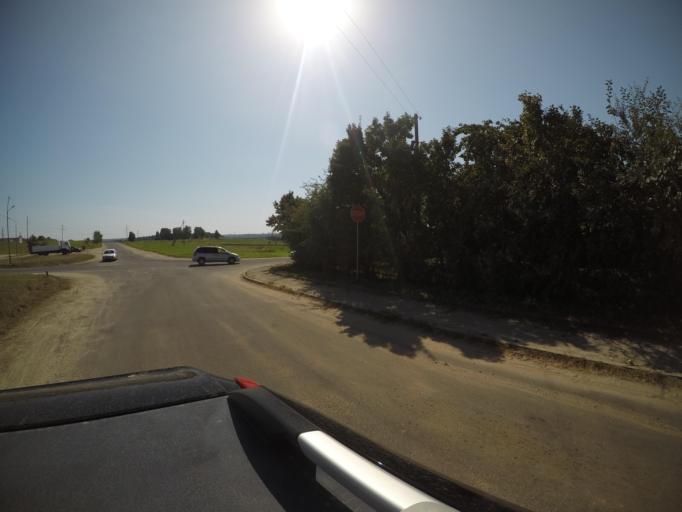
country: BY
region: Grodnenskaya
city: Hrodna
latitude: 53.7141
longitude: 23.8731
